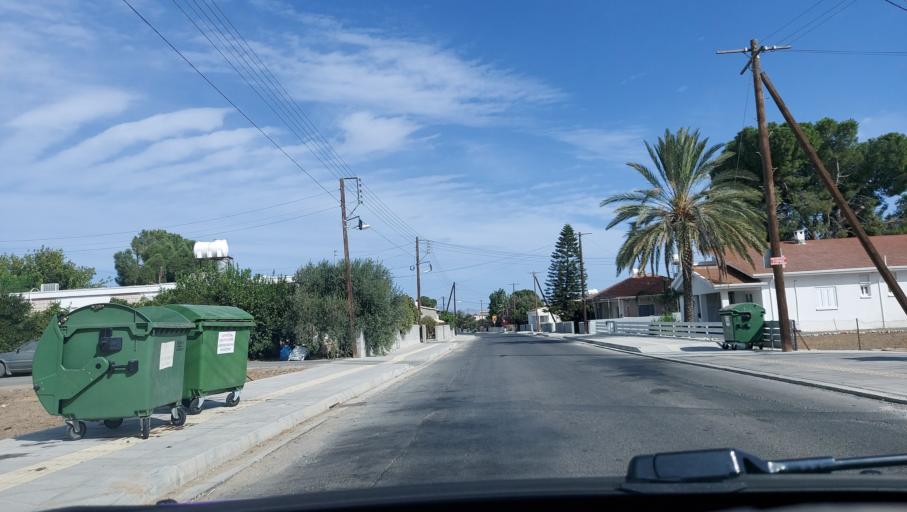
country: CY
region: Lefkosia
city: Pano Deftera
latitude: 35.0730
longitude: 33.2620
